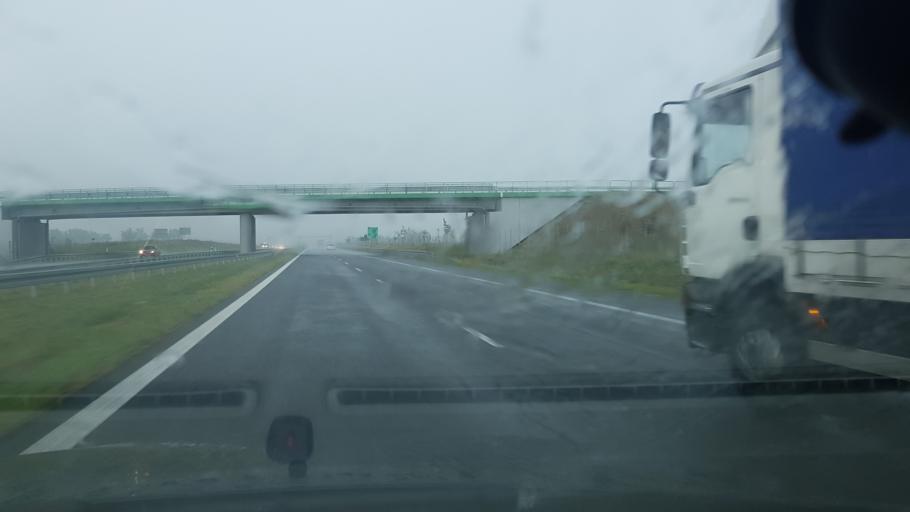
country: PL
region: Warmian-Masurian Voivodeship
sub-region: Powiat nidzicki
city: Nidzica
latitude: 53.3892
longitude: 20.3688
